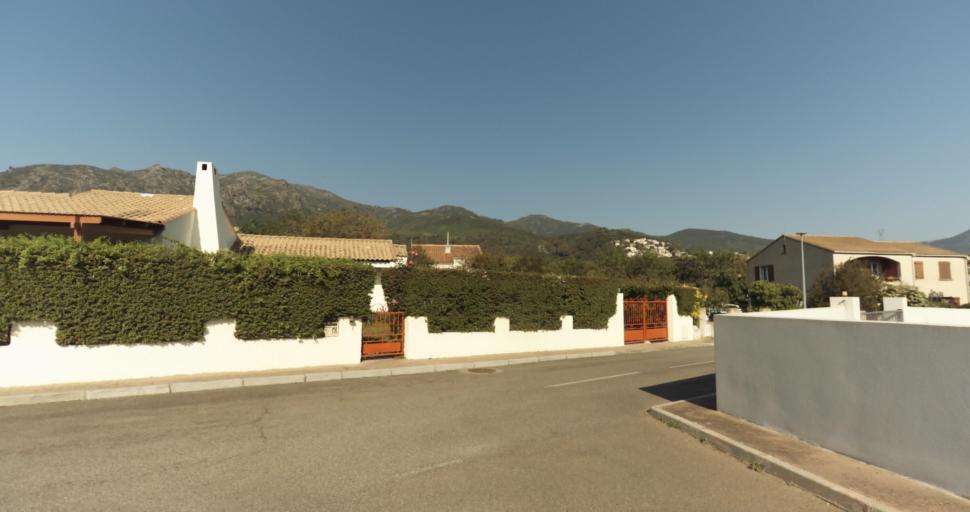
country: FR
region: Corsica
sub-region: Departement de la Haute-Corse
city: Biguglia
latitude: 42.6346
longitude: 9.4324
